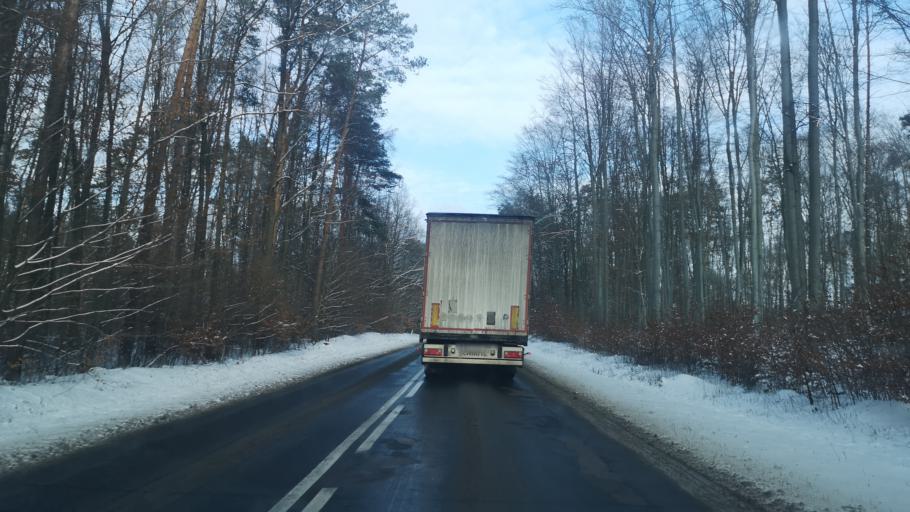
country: PL
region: Subcarpathian Voivodeship
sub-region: Powiat przeworski
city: Sieniawa
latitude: 50.2112
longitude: 22.6436
